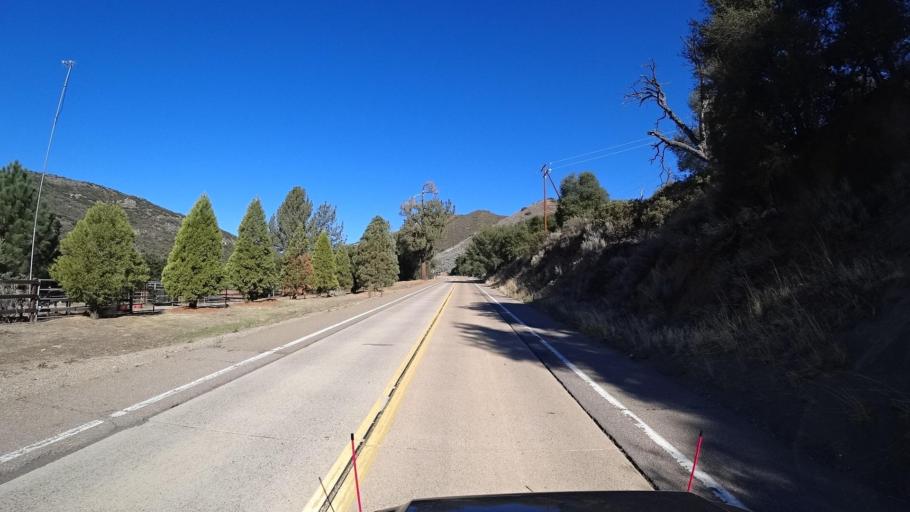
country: US
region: California
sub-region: San Diego County
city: Pine Valley
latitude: 32.8386
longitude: -116.5379
